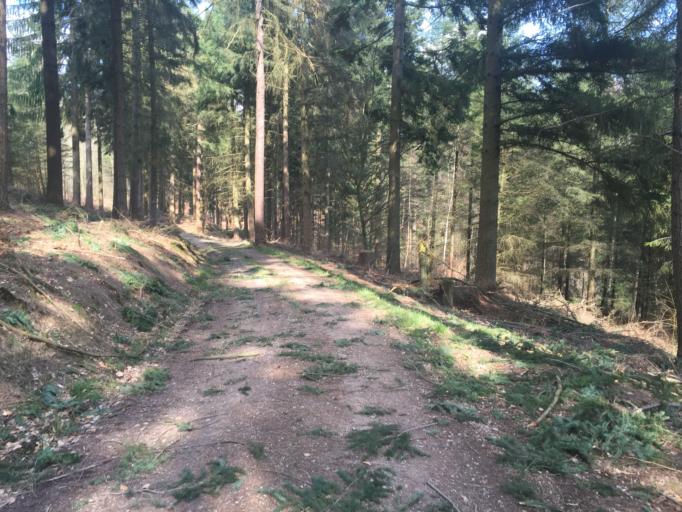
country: DE
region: Baden-Wuerttemberg
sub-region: Karlsruhe Region
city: Wilhelmsfeld
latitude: 49.4775
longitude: 8.7190
